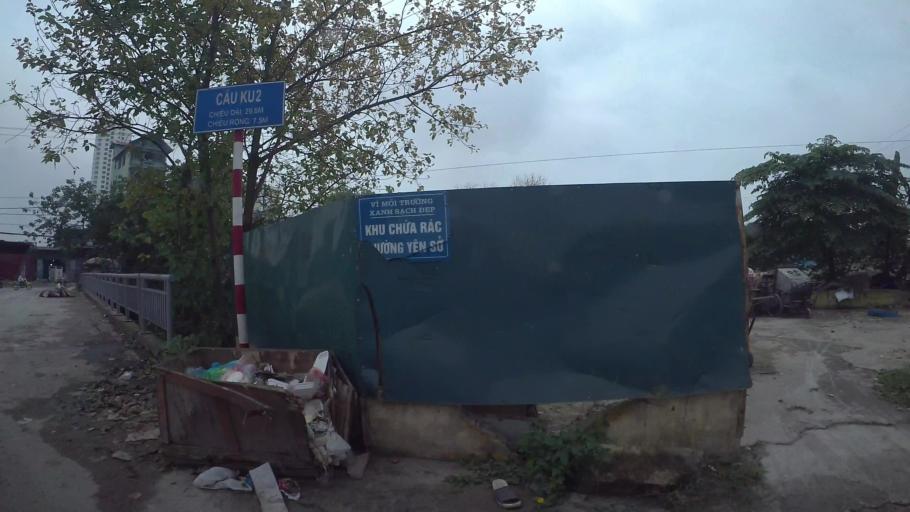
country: VN
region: Ha Noi
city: Van Dien
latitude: 20.9760
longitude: 105.8652
